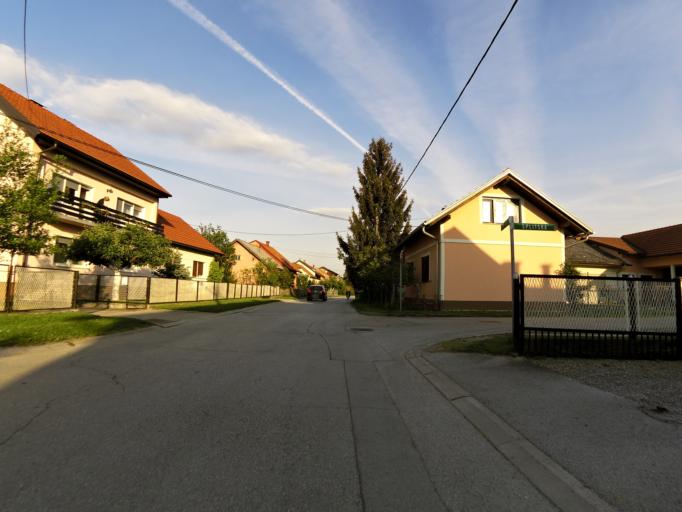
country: HR
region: Karlovacka
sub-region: Grad Karlovac
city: Karlovac
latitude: 45.4992
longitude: 15.5367
